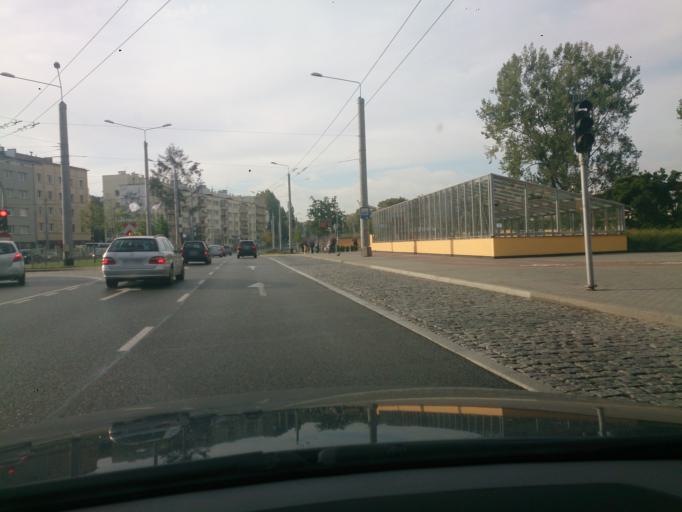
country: PL
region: Pomeranian Voivodeship
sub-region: Gdynia
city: Gdynia
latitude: 54.5082
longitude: 18.5366
